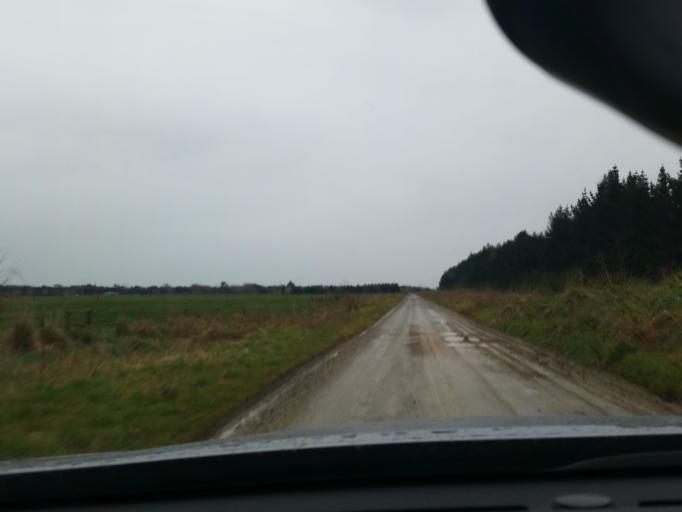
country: NZ
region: Southland
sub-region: Southland District
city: Winton
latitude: -46.2332
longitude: 168.4844
